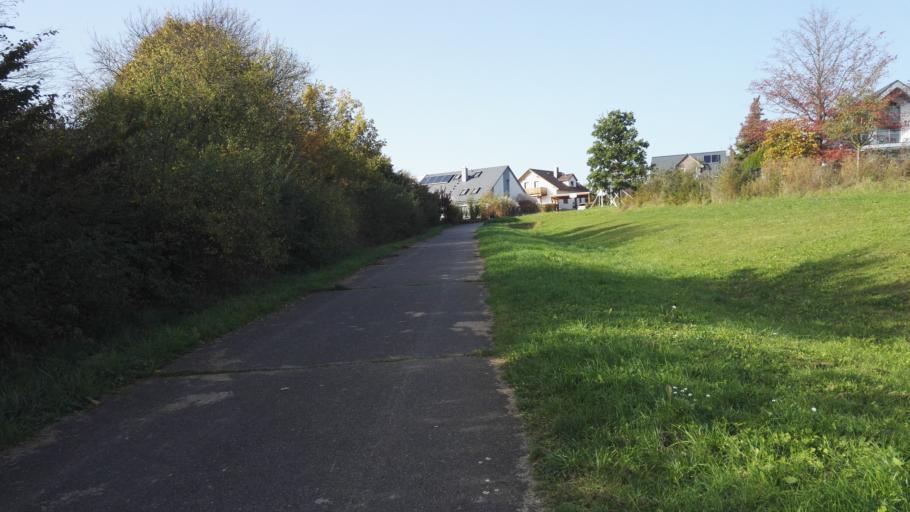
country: DE
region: Lower Saxony
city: Hildesheim
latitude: 52.1250
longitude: 9.9923
